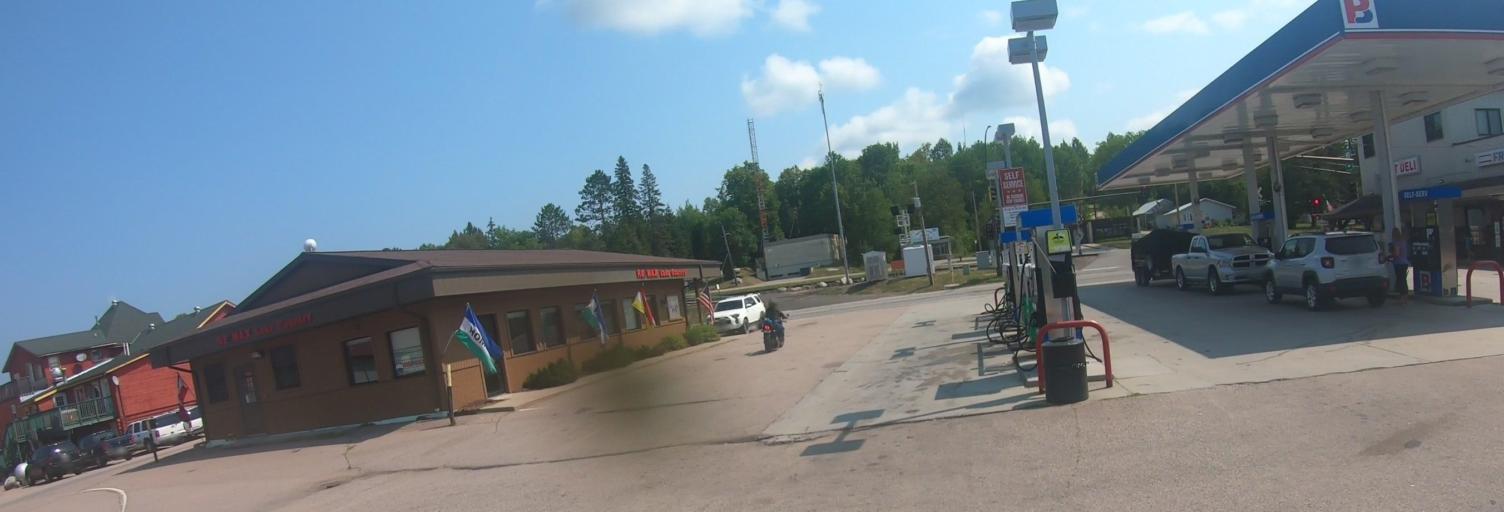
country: US
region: Minnesota
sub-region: Saint Louis County
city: Mountain Iron
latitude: 48.0538
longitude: -92.8322
